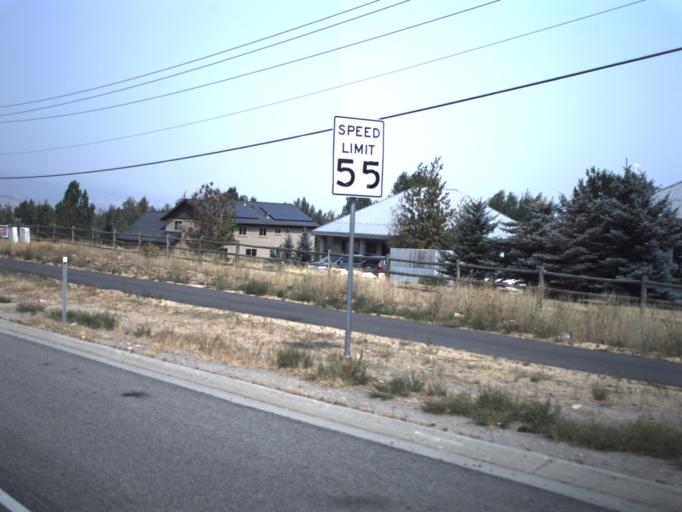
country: US
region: Utah
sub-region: Summit County
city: Snyderville
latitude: 40.6974
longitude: -111.5442
